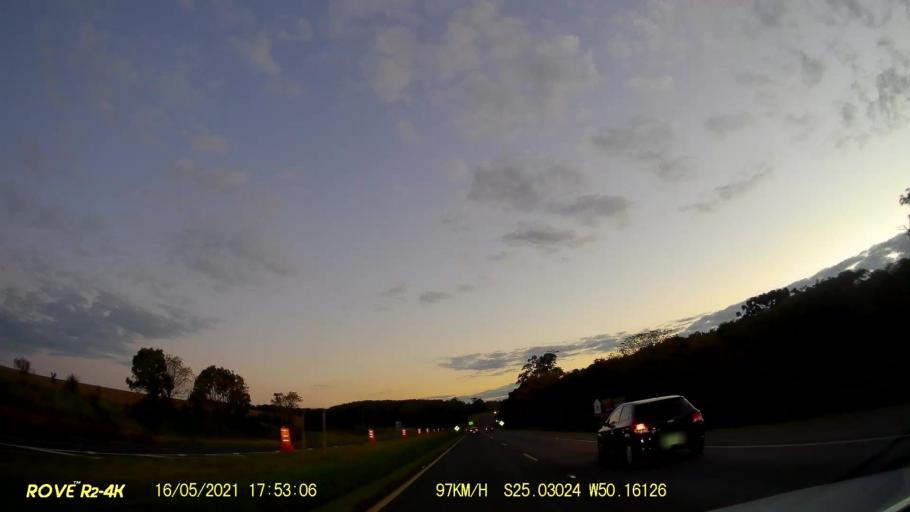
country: BR
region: Parana
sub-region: Ponta Grossa
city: Ponta Grossa
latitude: -25.0300
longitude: -50.1609
